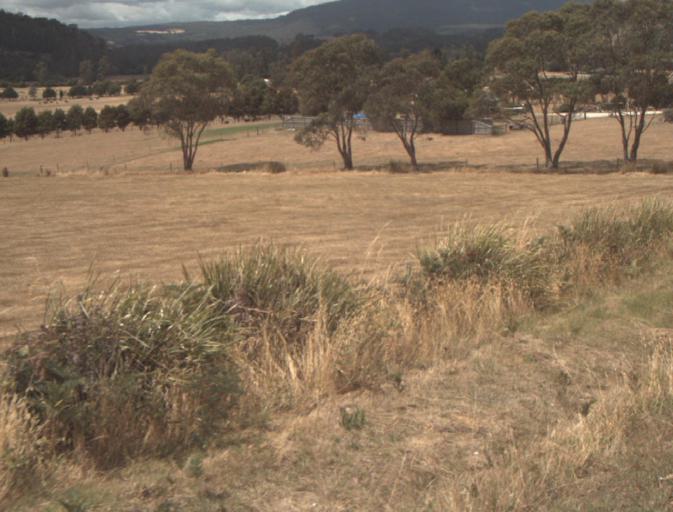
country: AU
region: Tasmania
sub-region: Launceston
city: Mayfield
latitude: -41.2344
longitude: 147.1482
